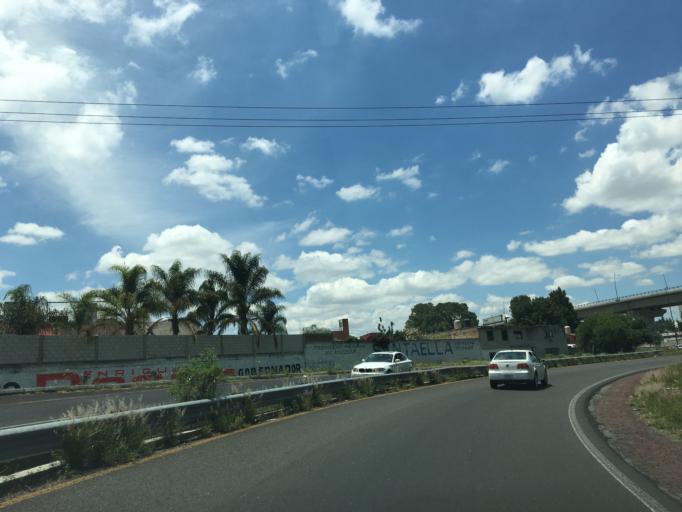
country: MX
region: Puebla
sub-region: Cuautlancingo
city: Sanctorum
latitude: 19.0981
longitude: -98.2283
